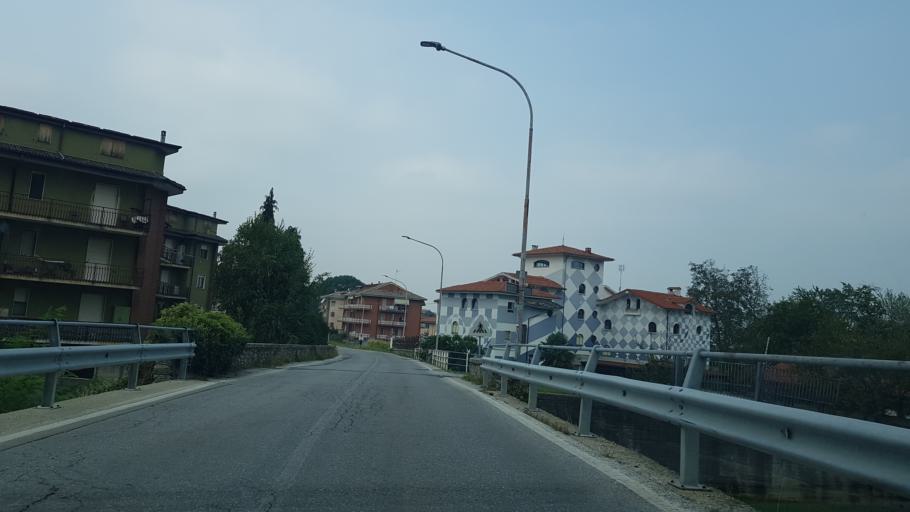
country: IT
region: Piedmont
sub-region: Provincia di Cuneo
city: Chiusa di Pesio
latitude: 44.3266
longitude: 7.6802
